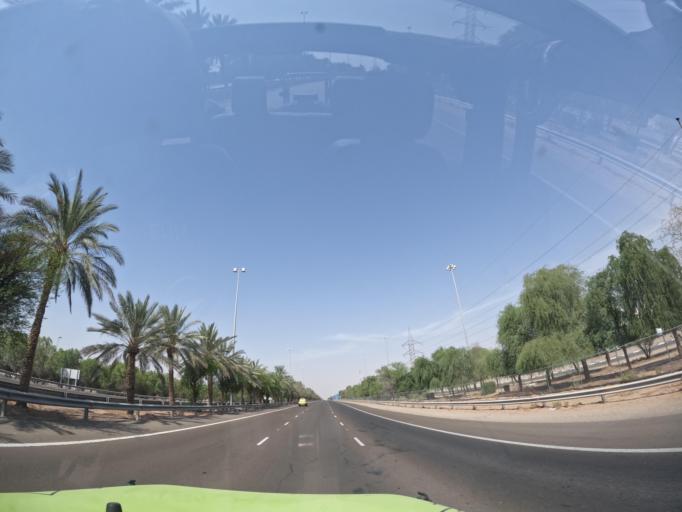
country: AE
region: Abu Dhabi
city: Al Ain
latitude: 24.2101
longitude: 55.5107
